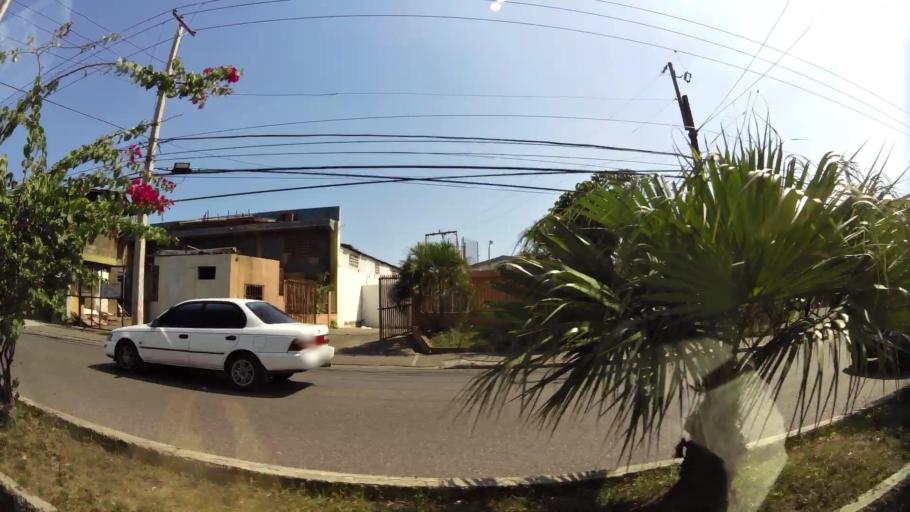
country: DO
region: Nacional
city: Santo Domingo
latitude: 18.4852
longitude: -69.9898
